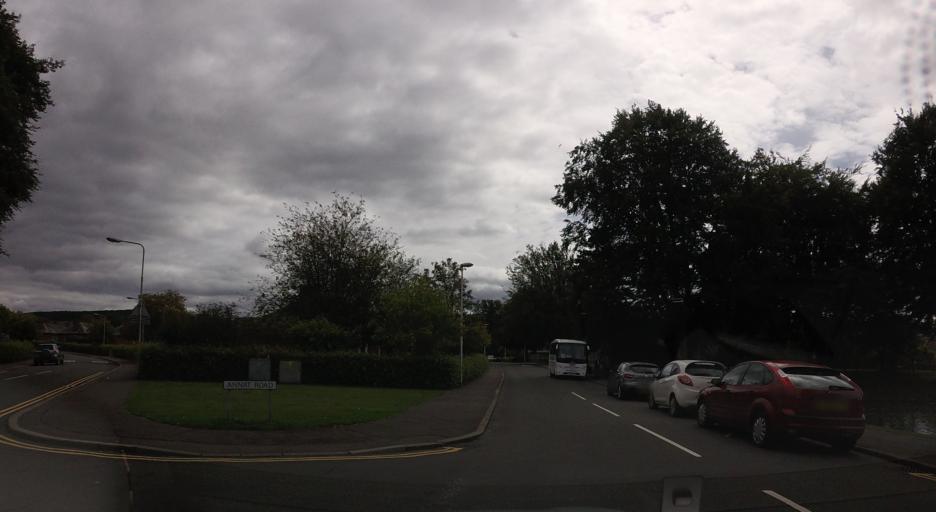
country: GB
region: Scotland
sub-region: Perth and Kinross
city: Perth
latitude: 56.4041
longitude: -3.4182
